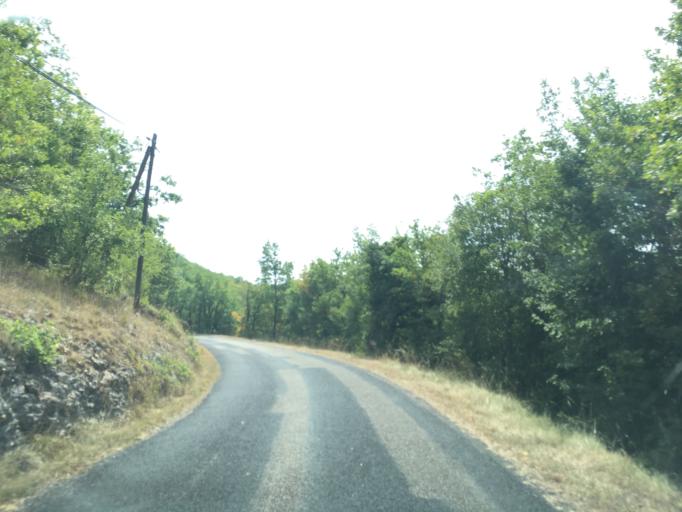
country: FR
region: Midi-Pyrenees
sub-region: Departement du Lot
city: Le Vigan
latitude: 44.7464
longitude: 1.5069
